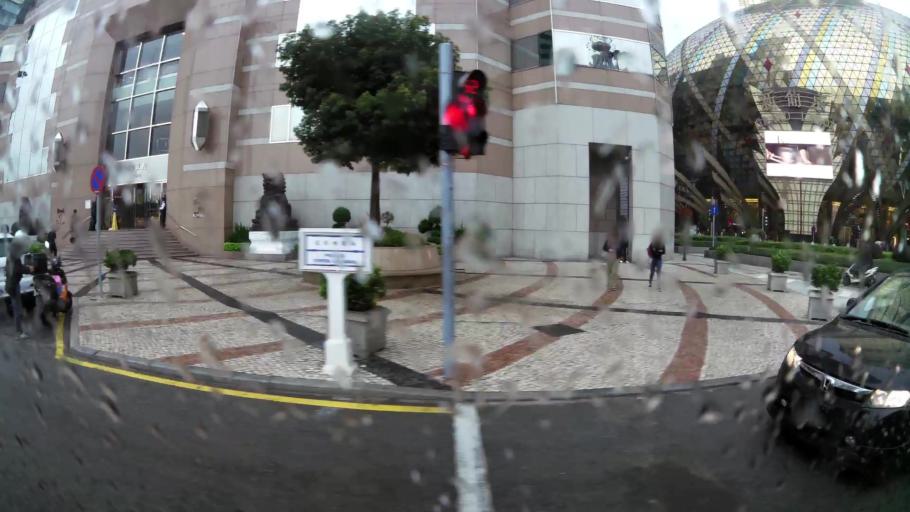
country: MO
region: Macau
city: Macau
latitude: 22.1898
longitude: 113.5434
